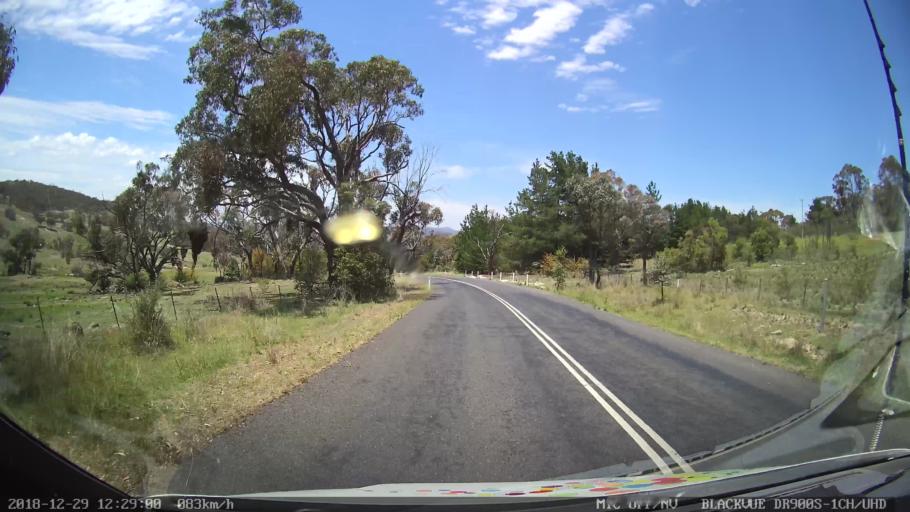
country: AU
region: Australian Capital Territory
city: Macarthur
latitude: -35.4927
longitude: 149.2284
